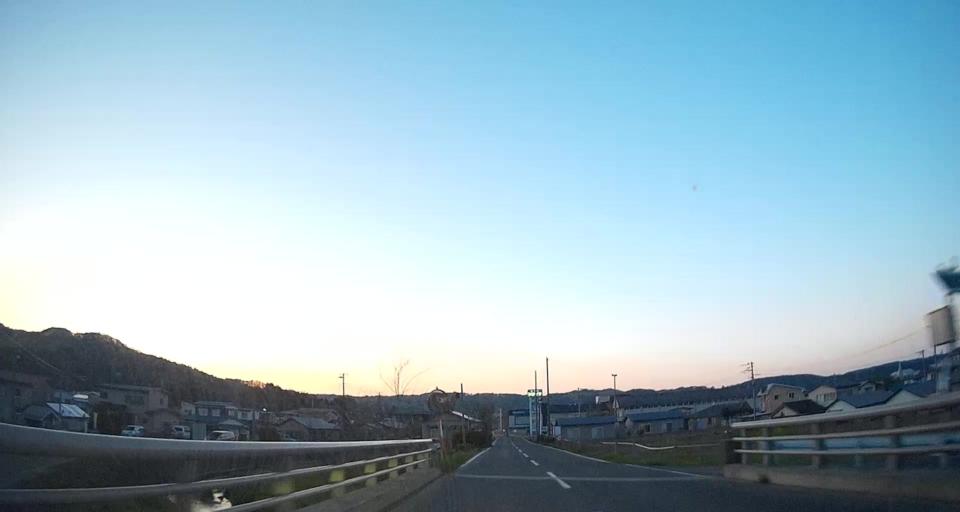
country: JP
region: Aomori
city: Hachinohe
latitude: 40.1817
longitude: 141.7733
